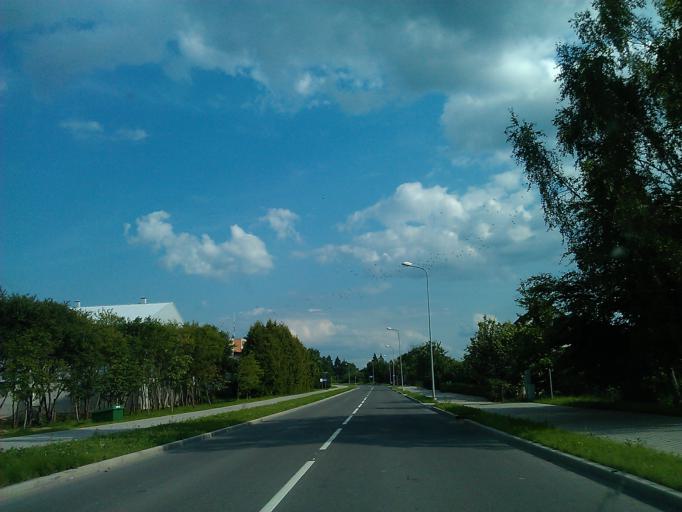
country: LV
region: Aizpute
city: Aizpute
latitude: 56.7100
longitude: 21.6187
